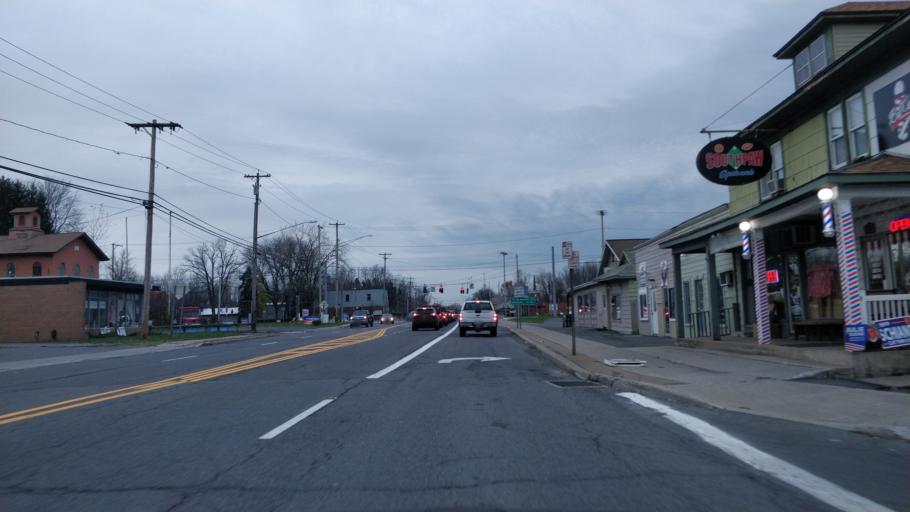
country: US
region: New York
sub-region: Onondaga County
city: North Syracuse
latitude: 43.1741
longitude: -76.1185
